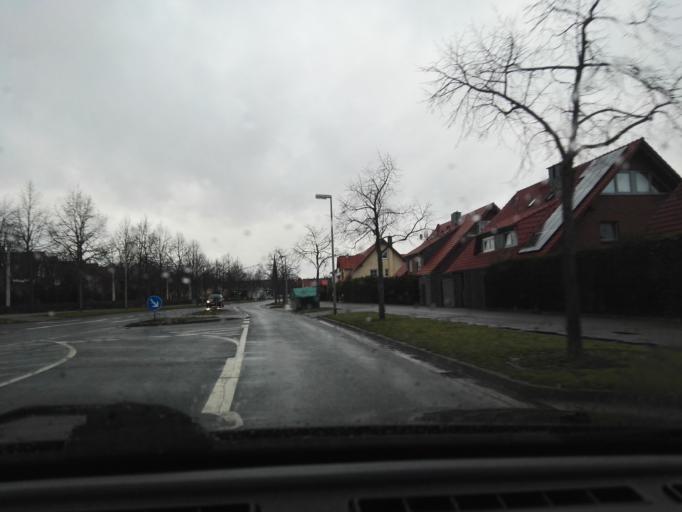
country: DE
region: Lower Saxony
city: Leiferde
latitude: 52.2341
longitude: 10.4850
